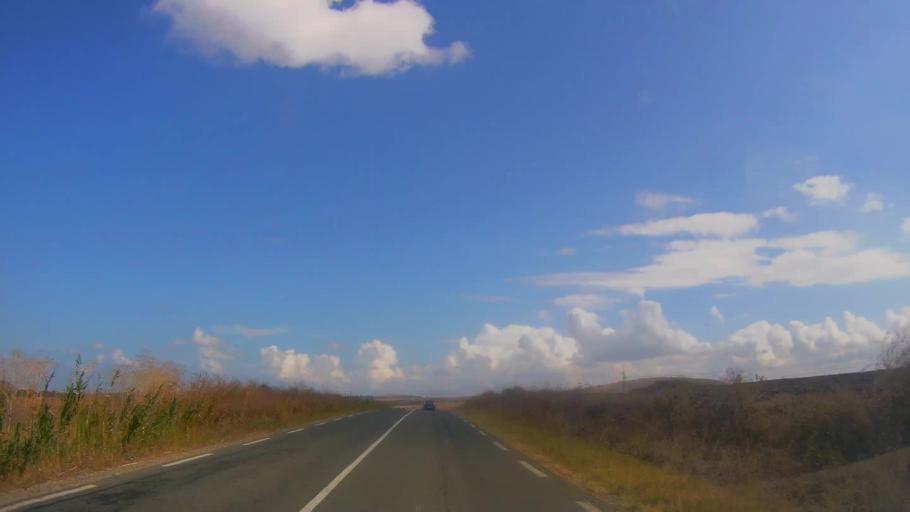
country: BG
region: Burgas
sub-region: Obshtina Kameno
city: Kameno
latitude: 42.4778
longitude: 27.3515
